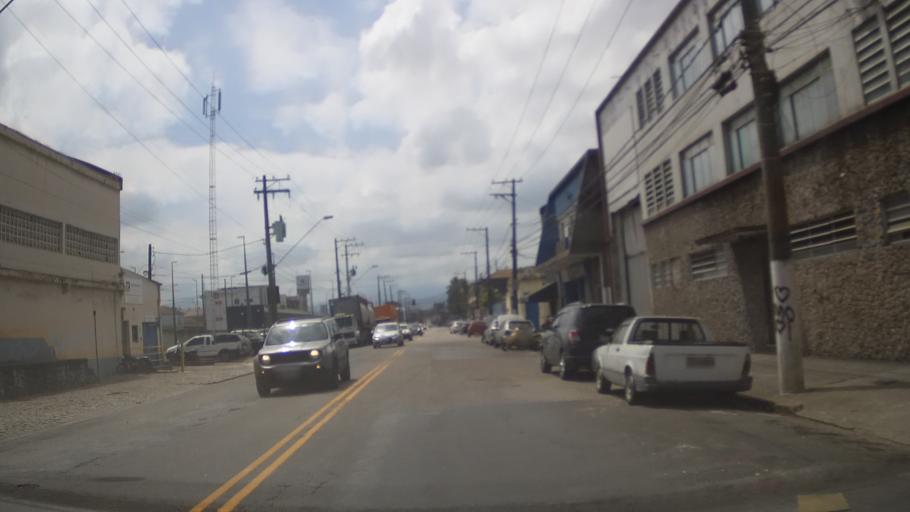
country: BR
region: Sao Paulo
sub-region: Santos
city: Santos
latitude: -23.9580
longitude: -46.3135
